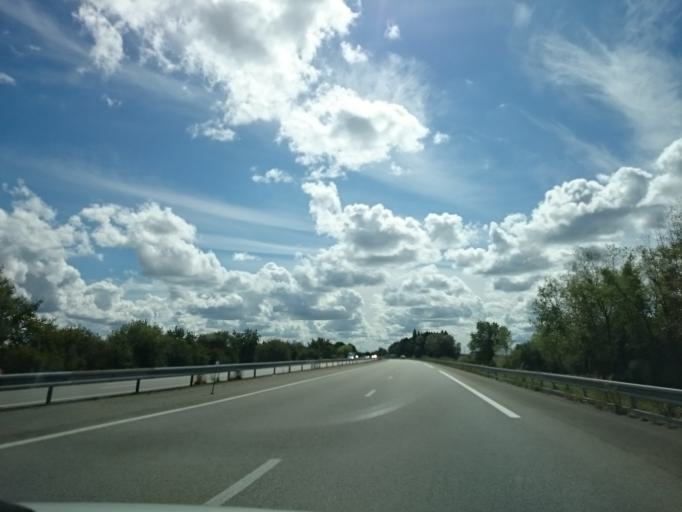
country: FR
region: Pays de la Loire
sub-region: Departement de la Loire-Atlantique
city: Mauves-sur-Loire
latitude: 47.3293
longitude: -1.4016
